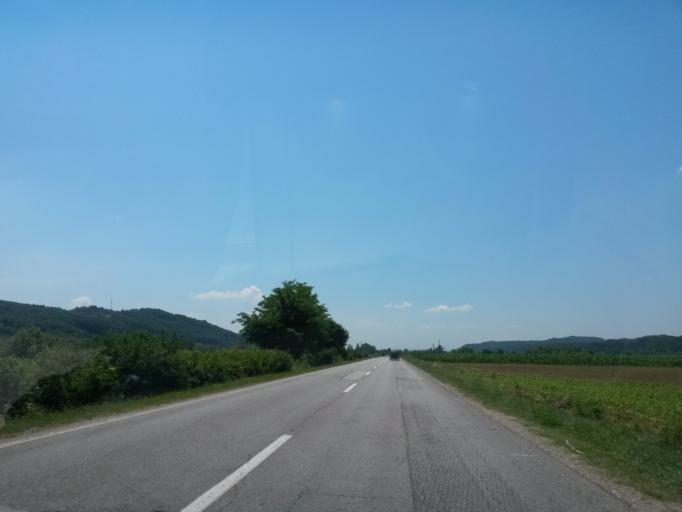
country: BA
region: Federation of Bosnia and Herzegovina
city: Lukavica
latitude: 44.9194
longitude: 18.1080
